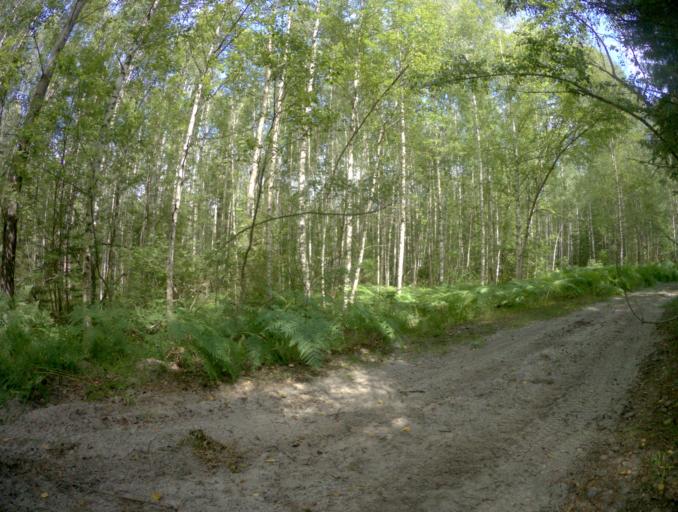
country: RU
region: Vladimir
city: Orgtrud
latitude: 56.0755
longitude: 40.6201
